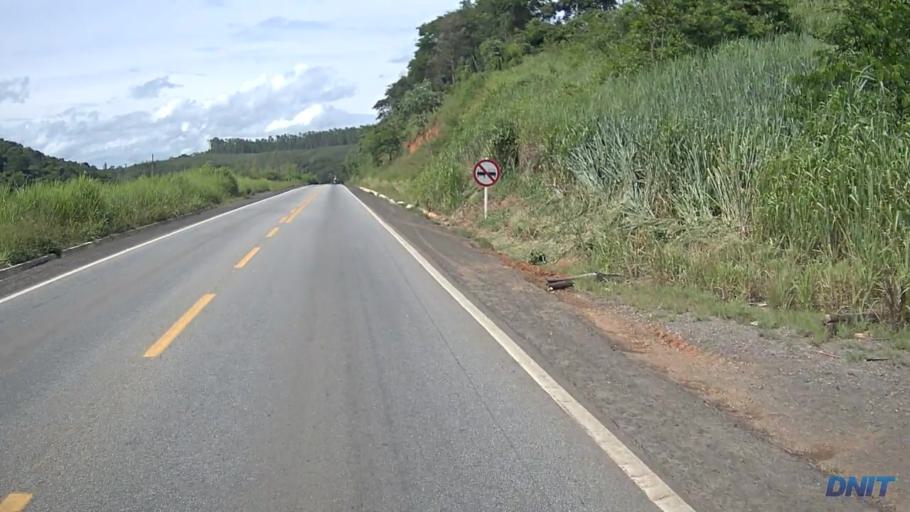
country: BR
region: Minas Gerais
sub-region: Ipaba
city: Ipaba
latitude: -19.4094
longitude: -42.4879
